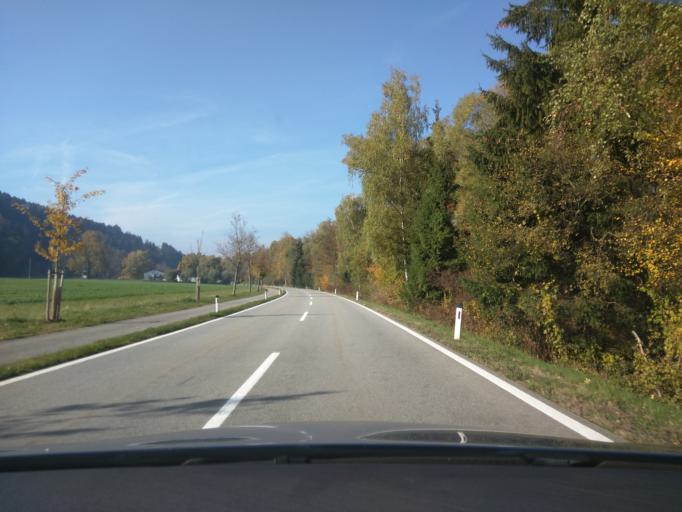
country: DE
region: Bavaria
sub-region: Lower Bavaria
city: Thyrnau
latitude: 48.5717
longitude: 13.5452
